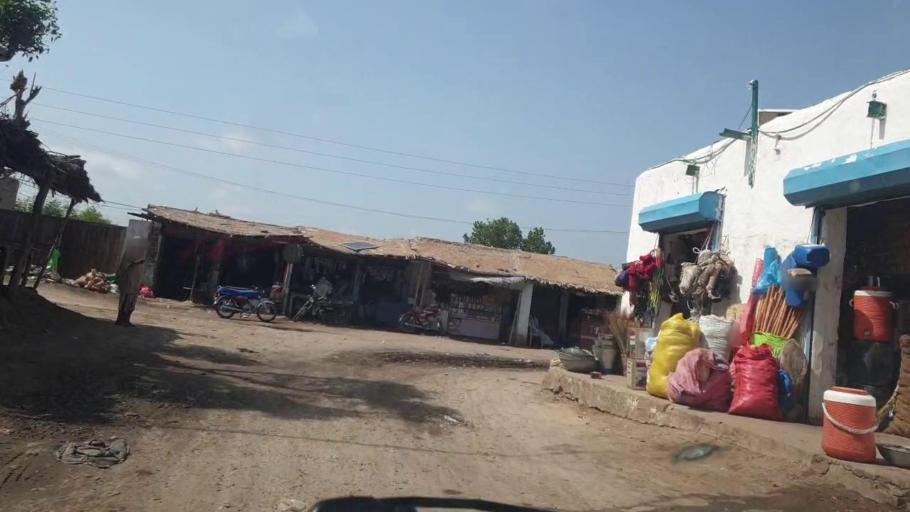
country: PK
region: Sindh
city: Berani
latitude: 25.7398
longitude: 68.9541
